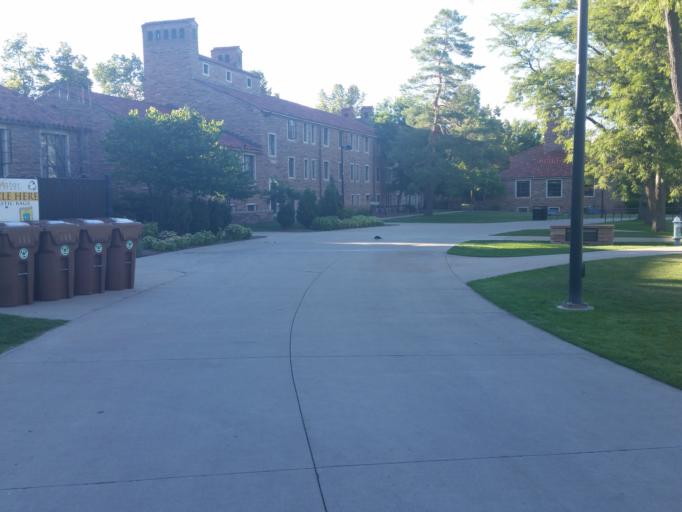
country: US
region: Colorado
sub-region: Boulder County
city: Boulder
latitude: 40.0057
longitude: -105.2644
